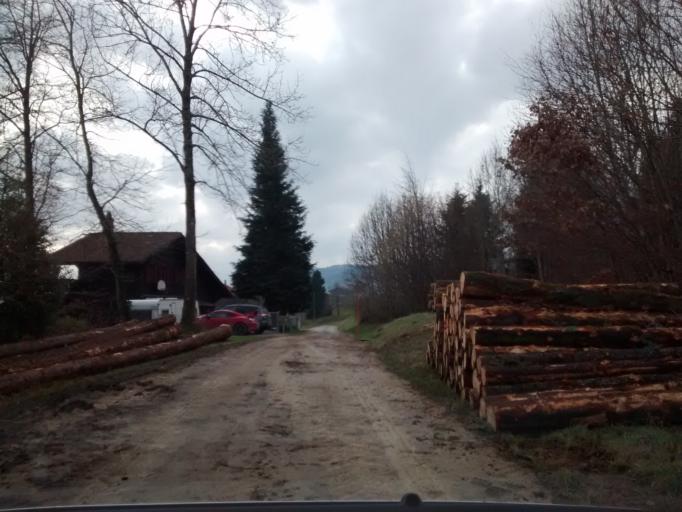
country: CH
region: Vaud
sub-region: Jura-Nord vaudois District
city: Orbe
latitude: 46.7531
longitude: 6.4769
